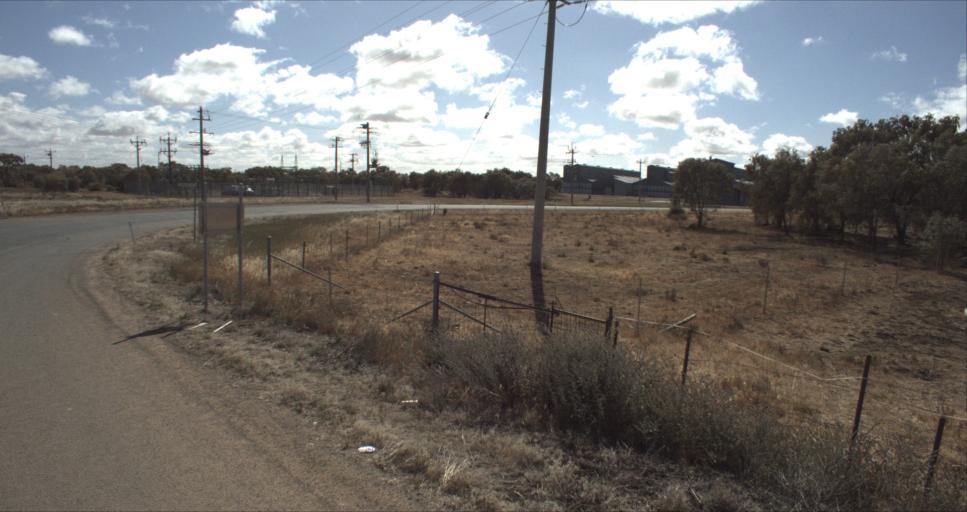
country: AU
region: New South Wales
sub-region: Murrumbidgee Shire
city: Darlington Point
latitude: -34.5140
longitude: 146.1770
